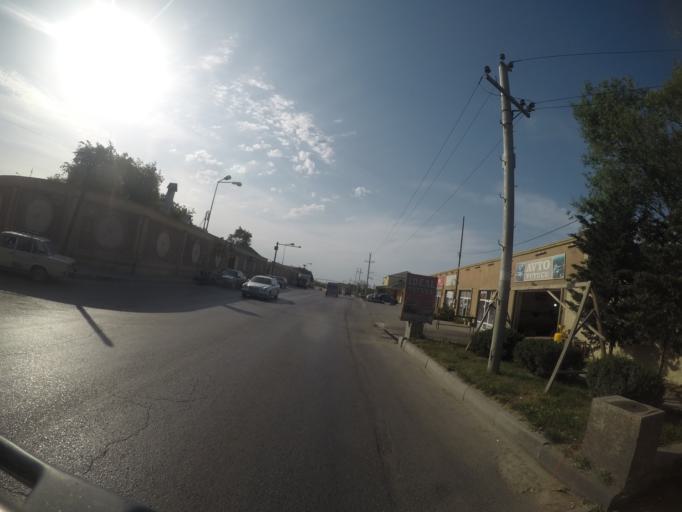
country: AZ
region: Baki
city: Binagadi
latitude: 40.4720
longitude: 49.8363
